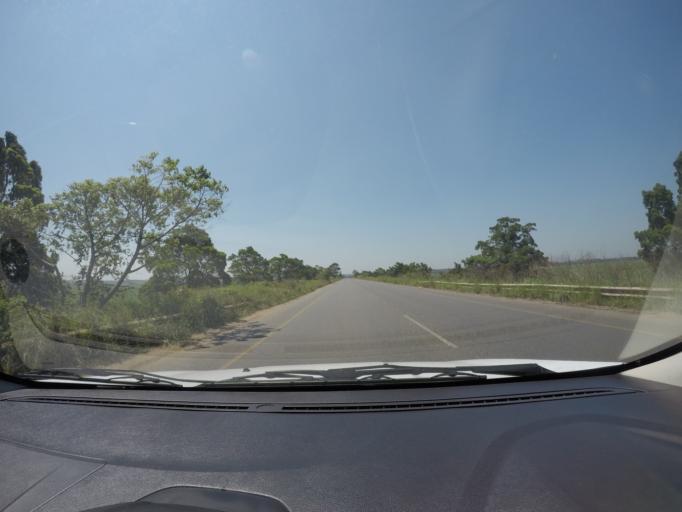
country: ZA
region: KwaZulu-Natal
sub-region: uThungulu District Municipality
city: Empangeni
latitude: -28.7959
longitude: 31.9582
